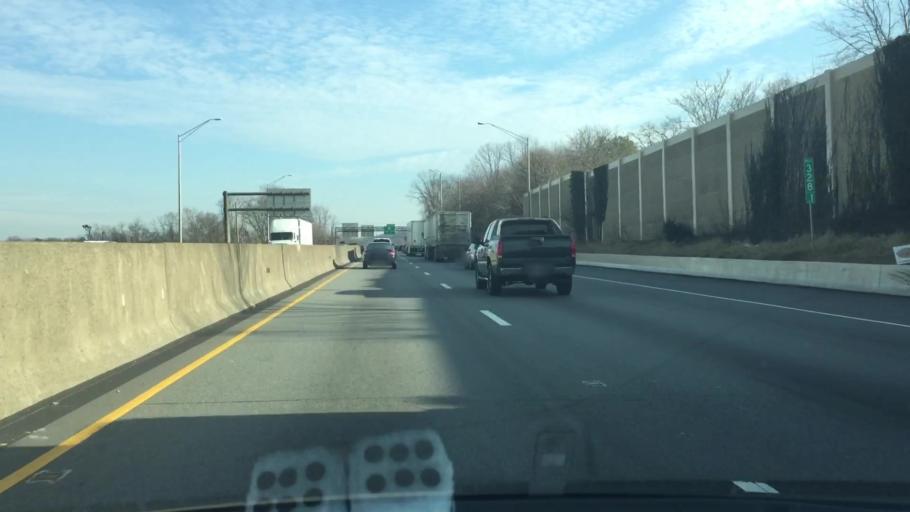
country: US
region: Pennsylvania
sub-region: Montgomery County
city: King of Prussia
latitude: 40.0797
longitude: -75.3806
